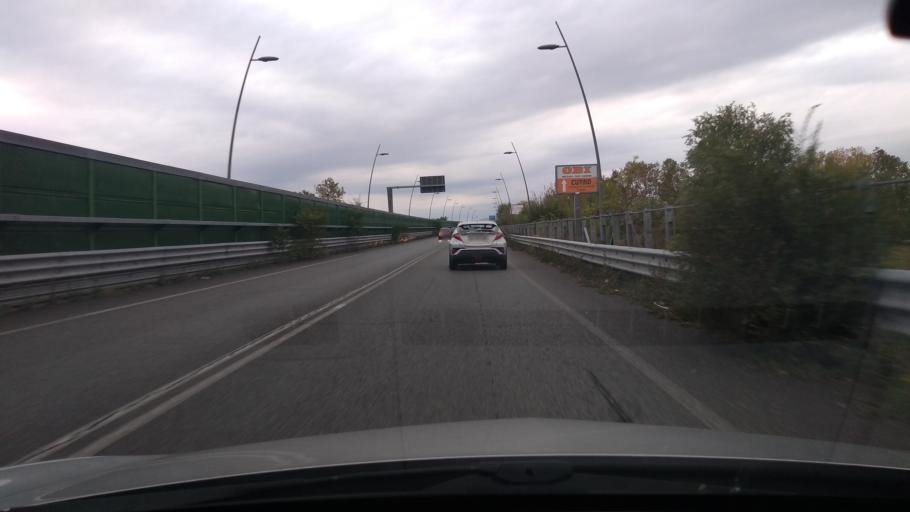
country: IT
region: Lombardy
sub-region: Provincia di Bergamo
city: Stezzano
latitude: 45.6399
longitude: 9.6398
